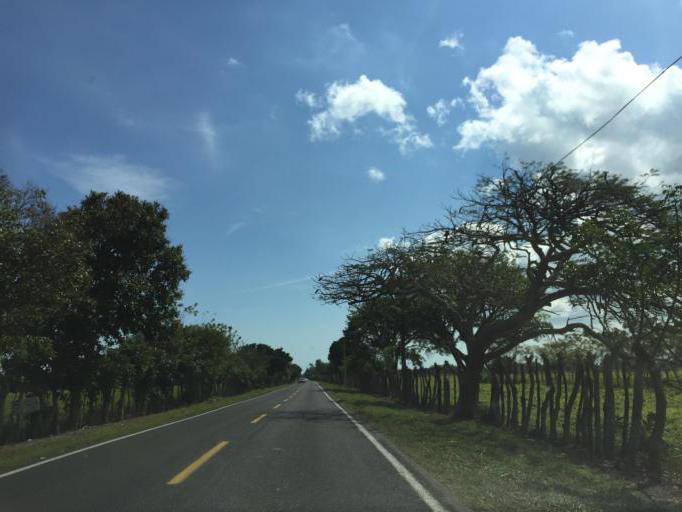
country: MX
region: Veracruz
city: Gutierrez Zamora
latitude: 20.4791
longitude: -97.0596
